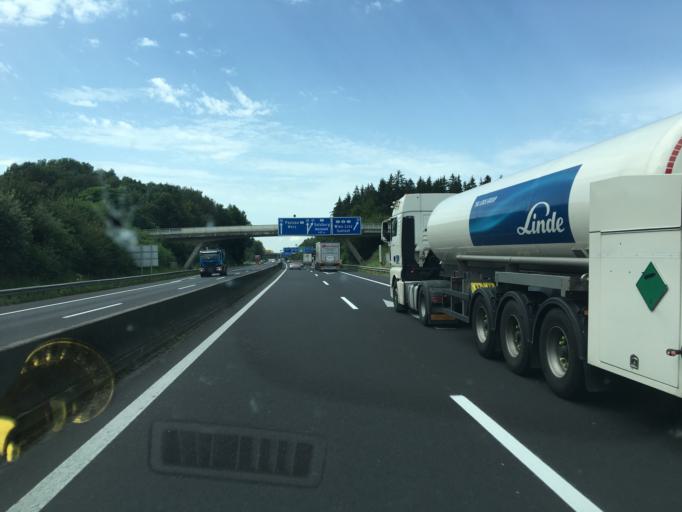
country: AT
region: Upper Austria
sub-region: Wels-Land
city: Sattledt
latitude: 48.0583
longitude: 14.0447
